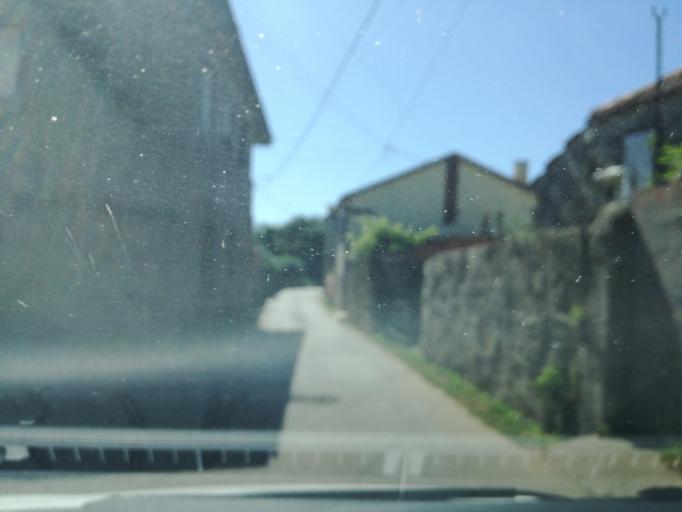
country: PT
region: Porto
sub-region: Matosinhos
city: Lavra
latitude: 41.2663
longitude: -8.7058
